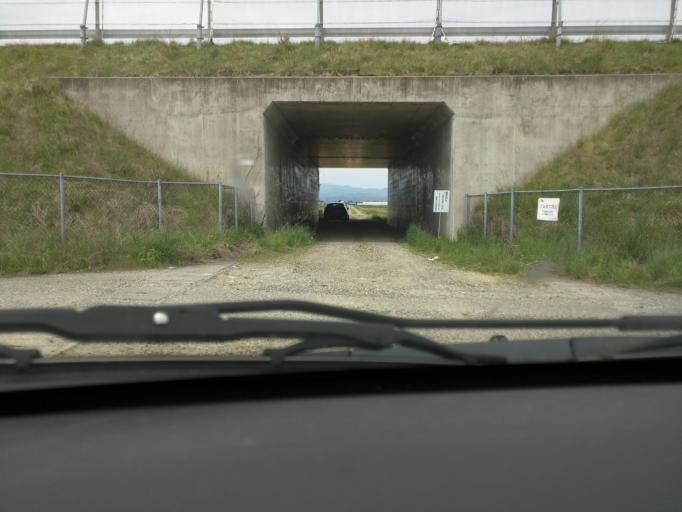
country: JP
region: Fukushima
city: Kitakata
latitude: 37.5300
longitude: 139.8653
